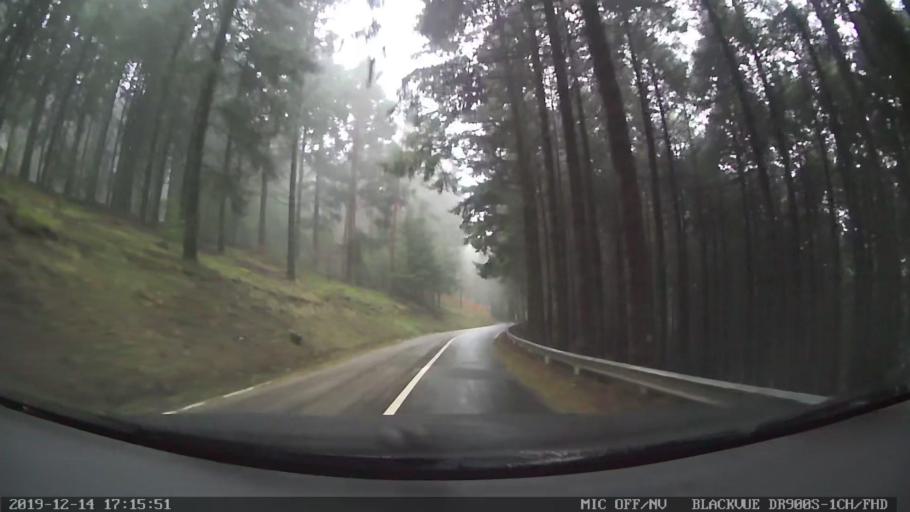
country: PT
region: Vila Real
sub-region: Vila Pouca de Aguiar
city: Vila Pouca de Aguiar
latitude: 41.5050
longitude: -7.6271
